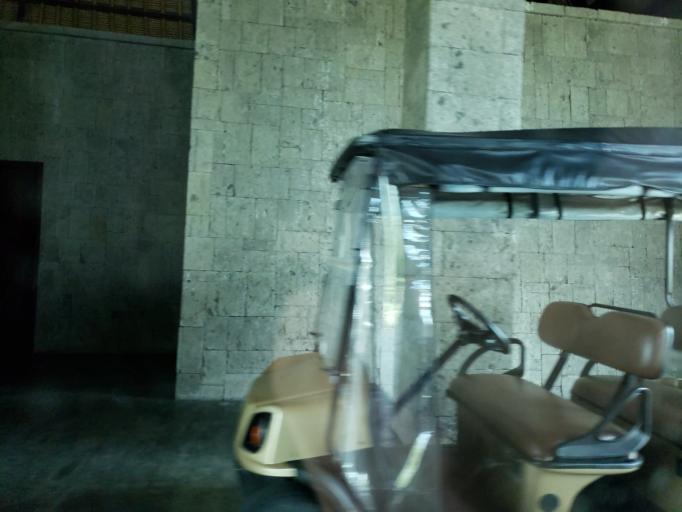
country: ID
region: Bali
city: Pecatu
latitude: -8.8439
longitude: 115.1208
